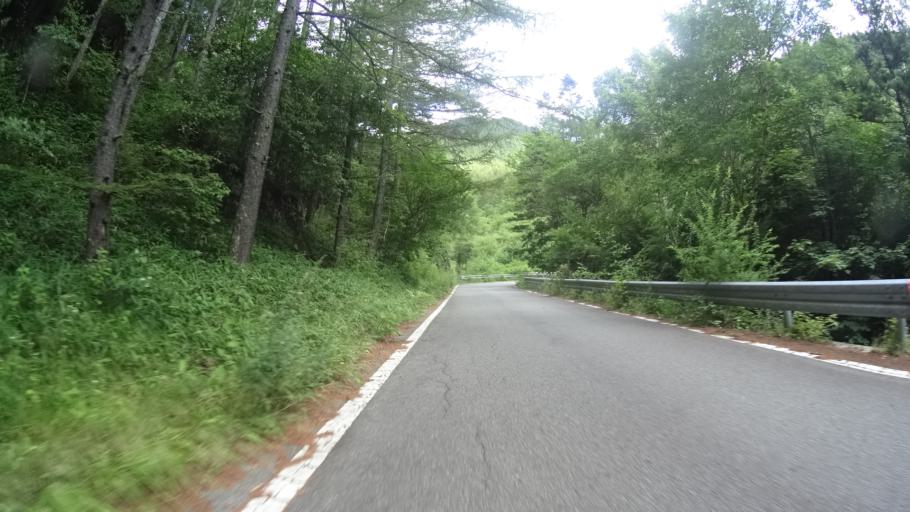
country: JP
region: Yamanashi
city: Enzan
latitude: 35.8396
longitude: 138.6444
